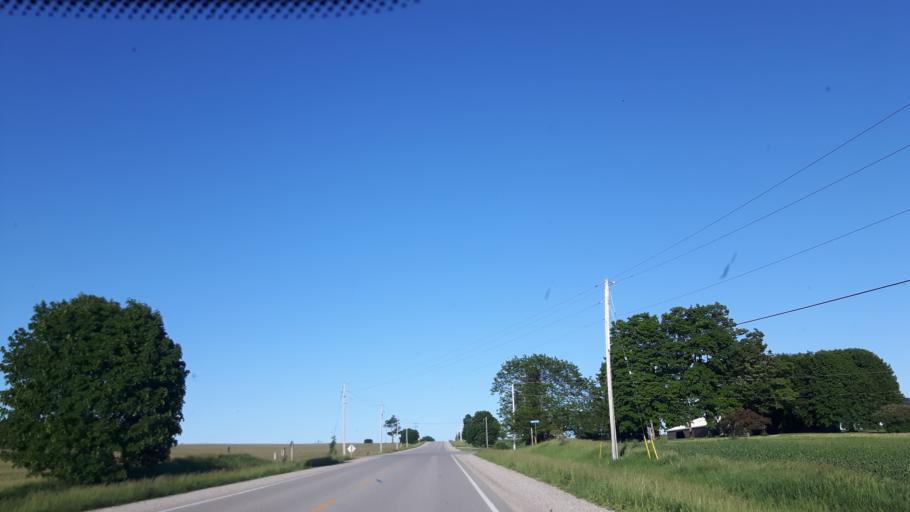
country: CA
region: Ontario
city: Goderich
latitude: 43.6427
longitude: -81.6245
